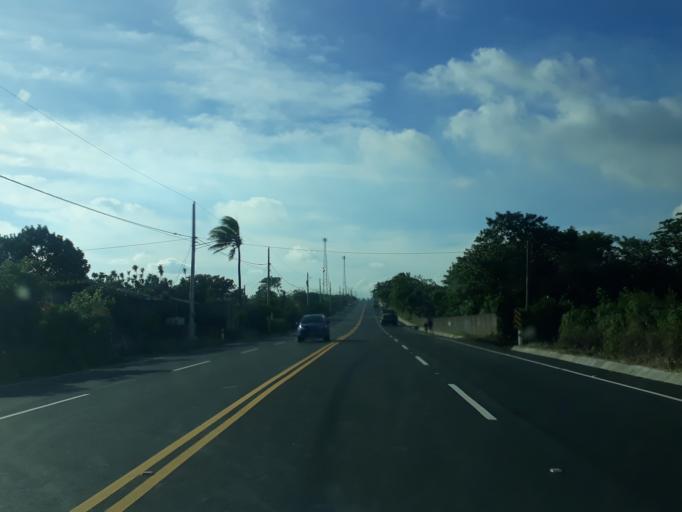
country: NI
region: Managua
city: El Crucero
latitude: 11.9214
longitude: -86.2796
